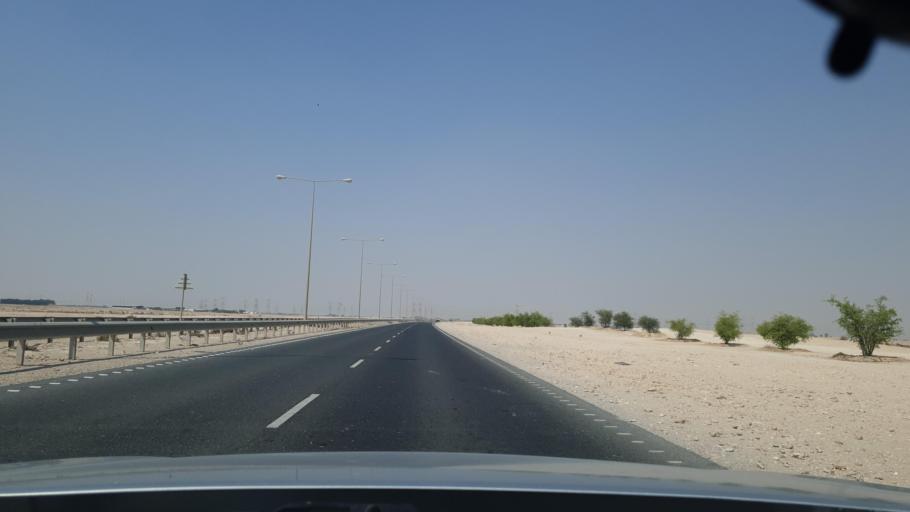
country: QA
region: Al Khawr
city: Al Khawr
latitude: 25.7392
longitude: 51.4886
